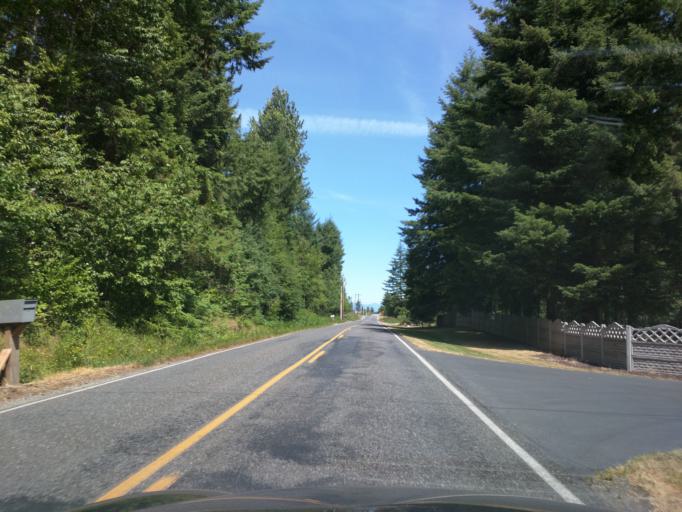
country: US
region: Washington
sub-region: Whatcom County
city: Geneva
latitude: 48.8303
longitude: -122.3987
